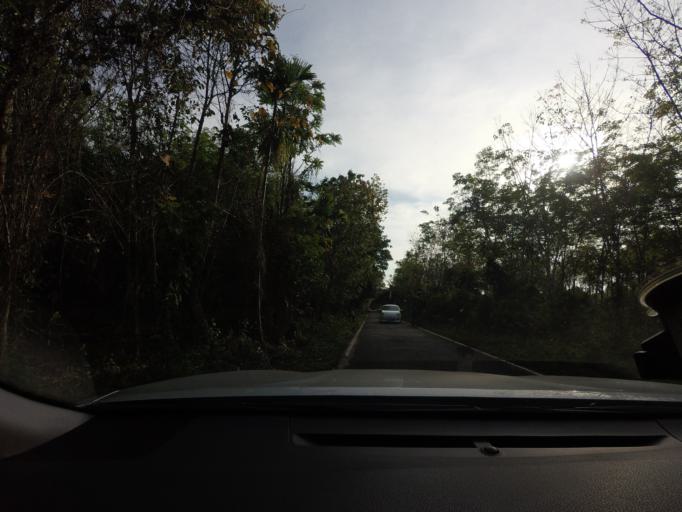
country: TH
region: Narathiwat
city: Ra-ngae
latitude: 6.3022
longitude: 101.7724
